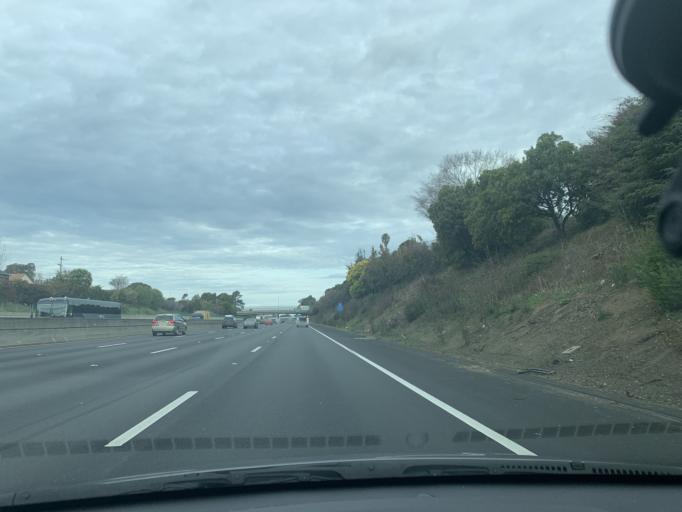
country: US
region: California
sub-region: Contra Costa County
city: East Richmond Heights
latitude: 37.9458
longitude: -122.3245
